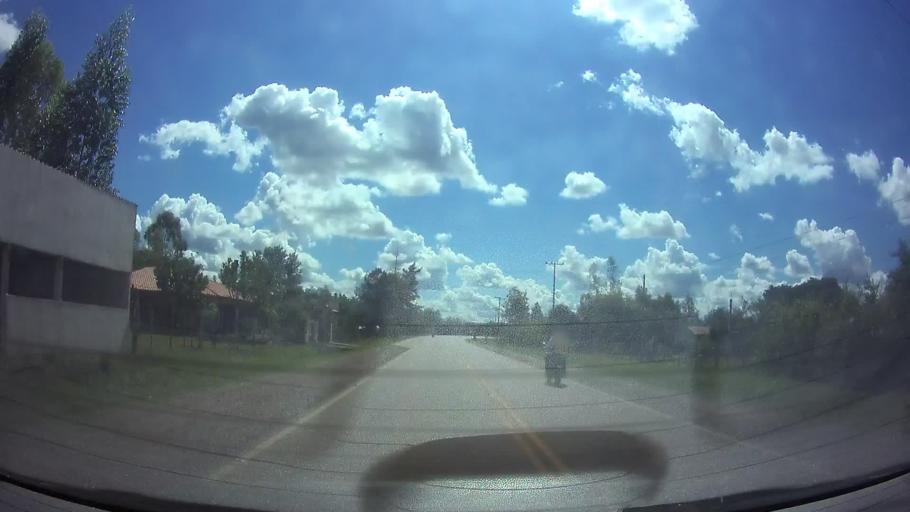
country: PY
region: Guaira
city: Itape
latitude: -25.9166
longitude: -56.6904
